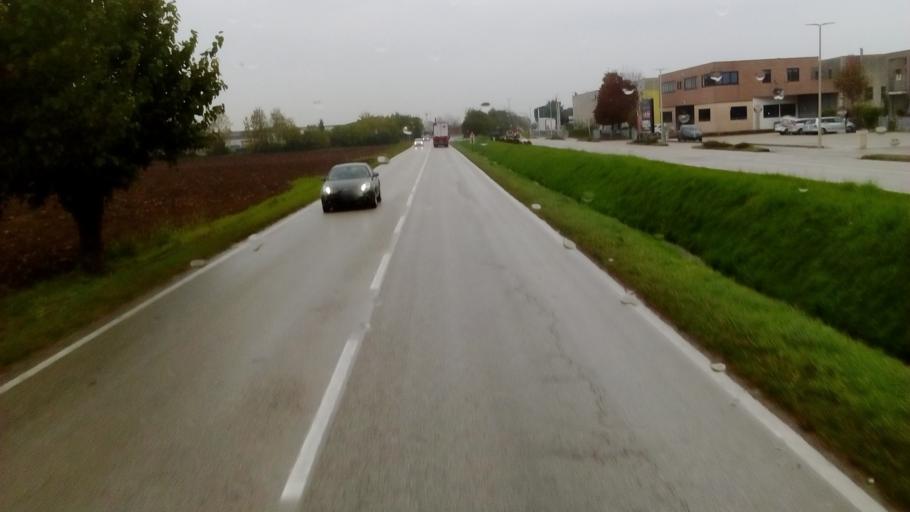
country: IT
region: Veneto
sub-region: Provincia di Vicenza
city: Montecchio Precalcino
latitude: 45.6664
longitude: 11.5769
